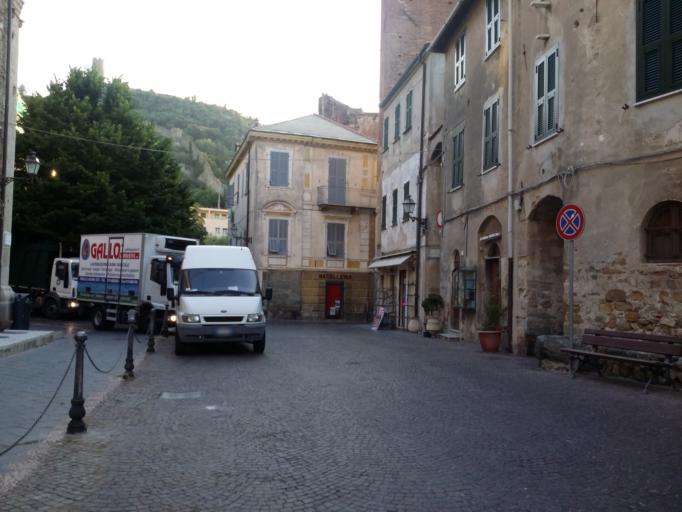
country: IT
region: Liguria
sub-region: Provincia di Savona
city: Noli
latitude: 44.2052
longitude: 8.4145
